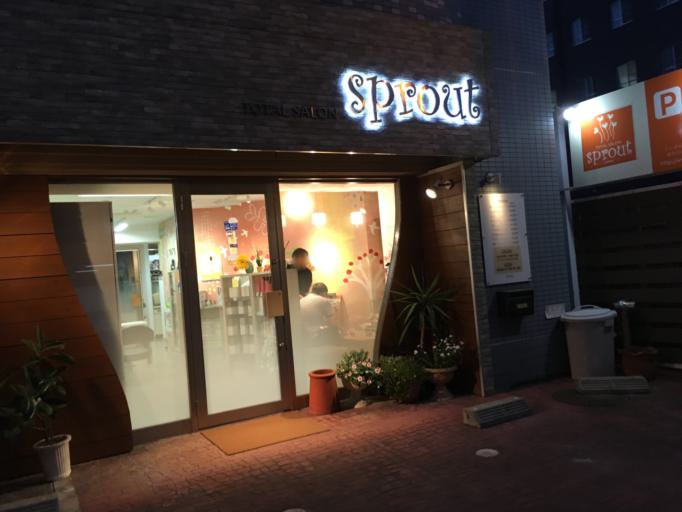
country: JP
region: Kumamoto
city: Kumamoto
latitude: 32.7947
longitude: 130.7281
